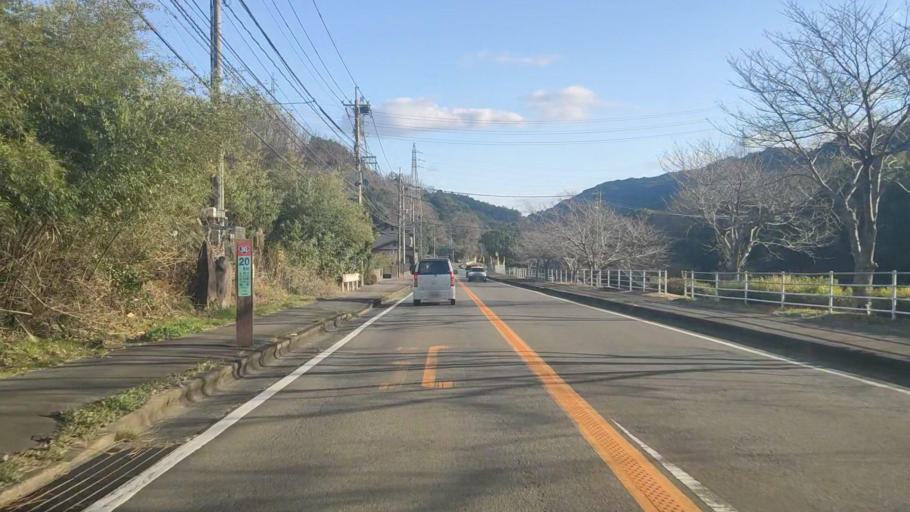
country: JP
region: Saga Prefecture
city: Saga-shi
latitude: 33.3385
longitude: 130.2590
